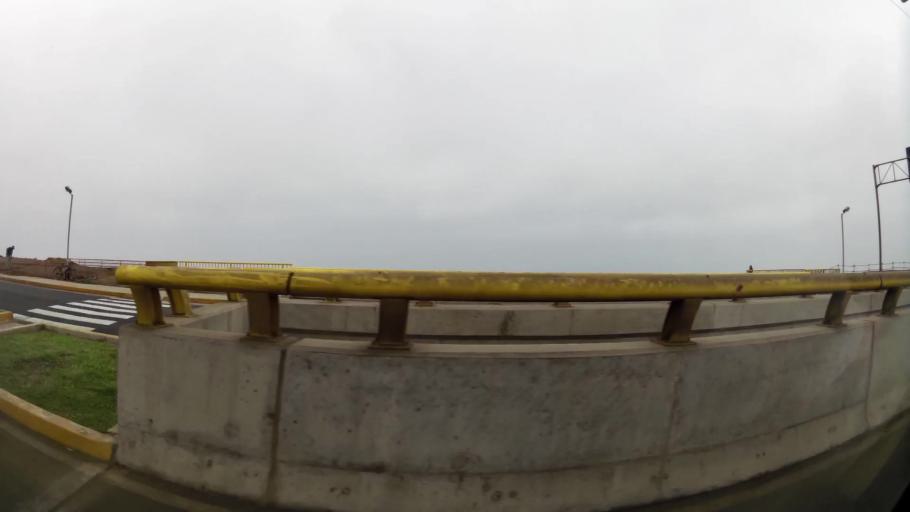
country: PE
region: Callao
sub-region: Callao
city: Callao
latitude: -12.0777
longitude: -77.1137
